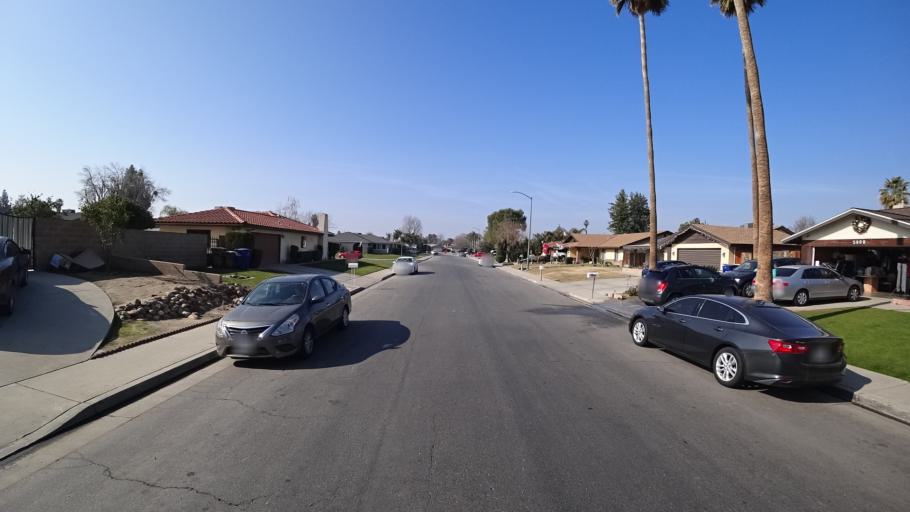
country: US
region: California
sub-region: Kern County
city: Bakersfield
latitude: 35.3324
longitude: -119.0676
